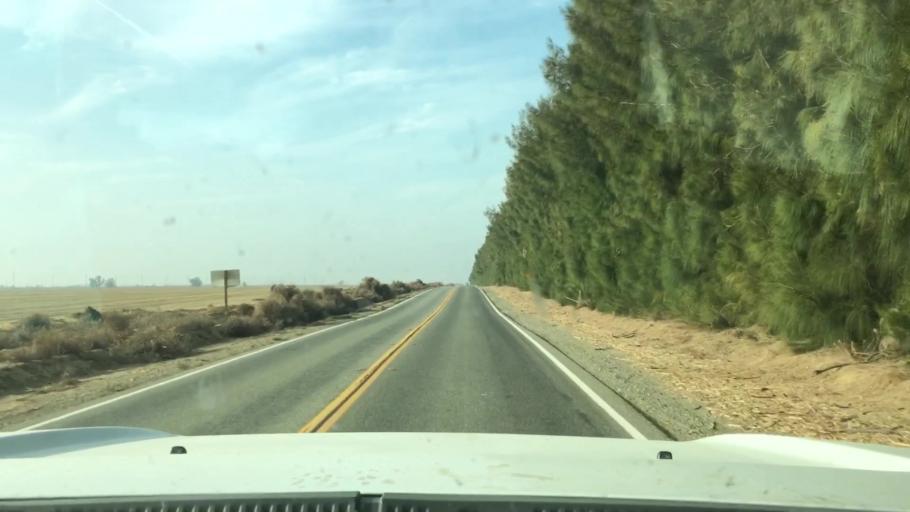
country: US
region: California
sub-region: Kern County
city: Lost Hills
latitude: 35.5012
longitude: -119.7410
